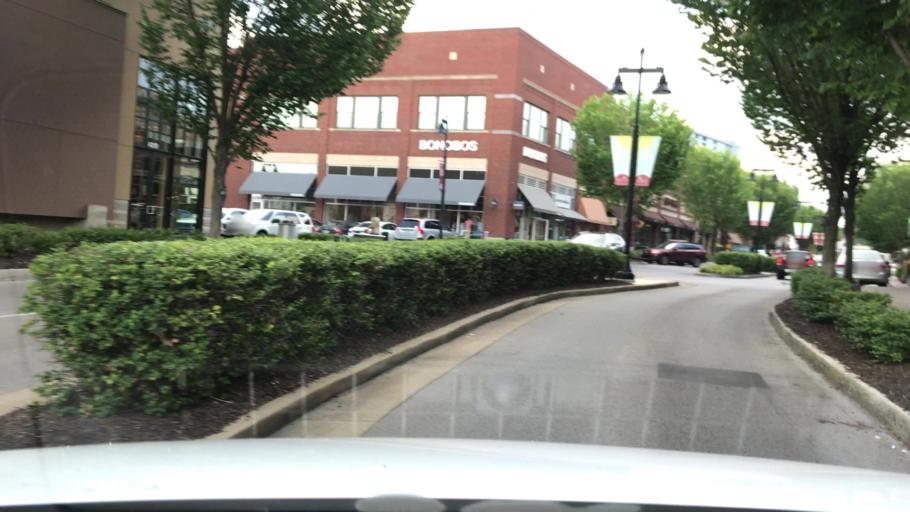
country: US
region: Tennessee
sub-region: Davidson County
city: Belle Meade
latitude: 36.1035
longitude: -86.8193
